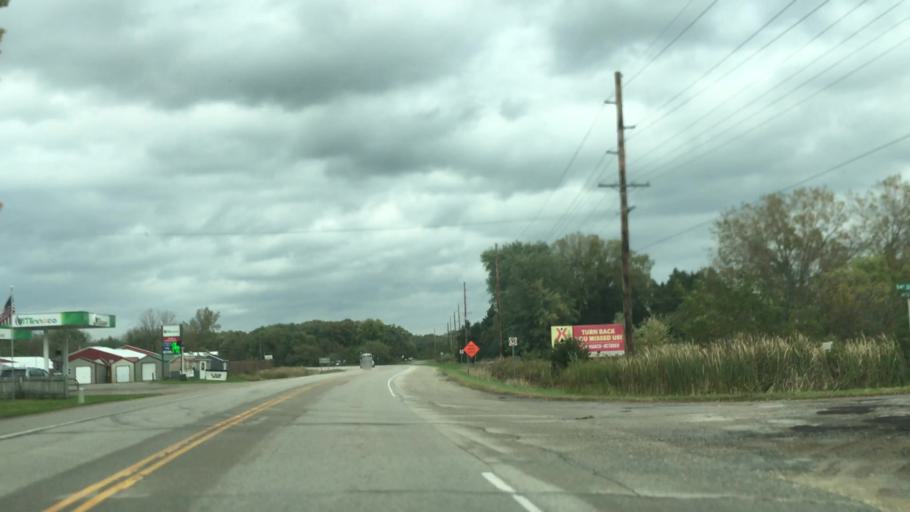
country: US
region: Minnesota
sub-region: Olmsted County
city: Eyota
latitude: 43.9434
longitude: -92.3507
